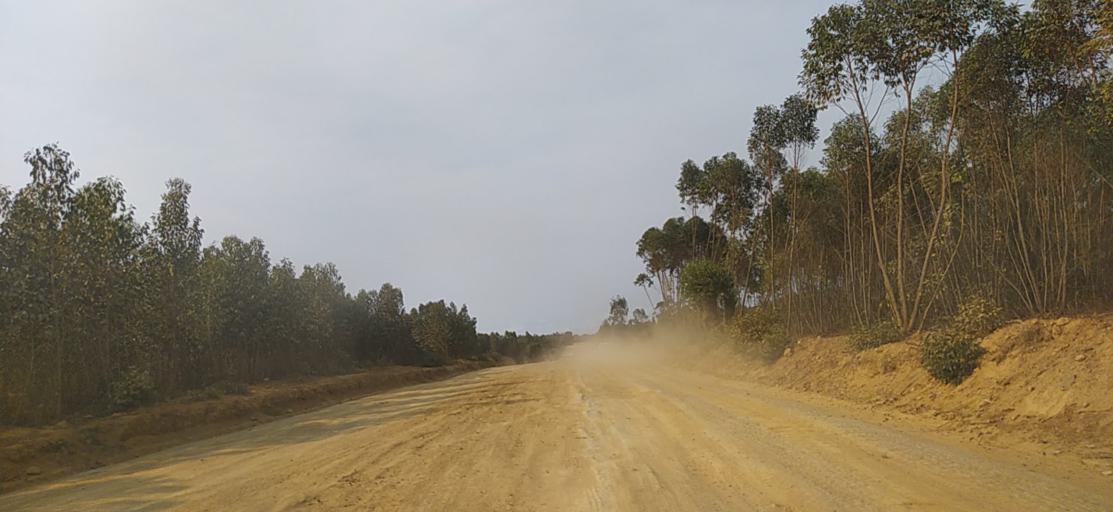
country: MG
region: Alaotra Mangoro
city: Moramanga
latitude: -18.6604
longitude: 48.2739
